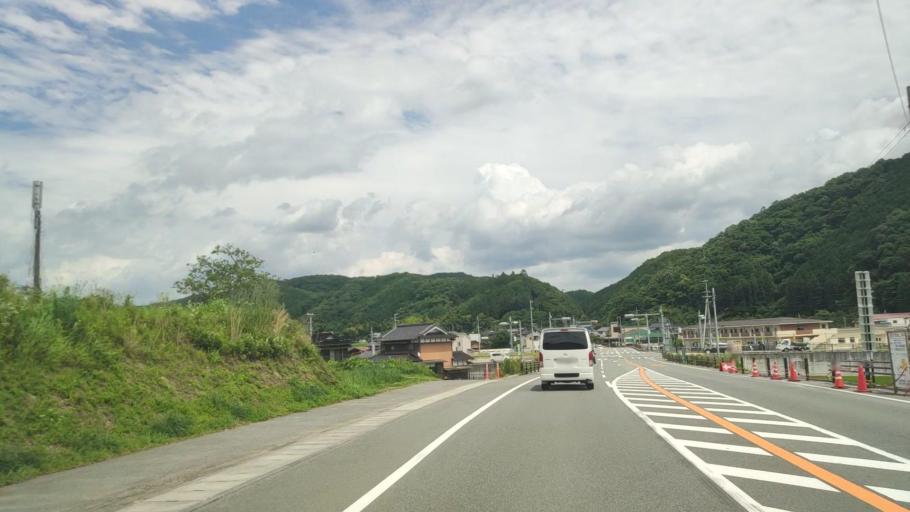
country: JP
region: Hyogo
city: Yamazakicho-nakabirose
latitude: 34.9944
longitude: 134.3932
